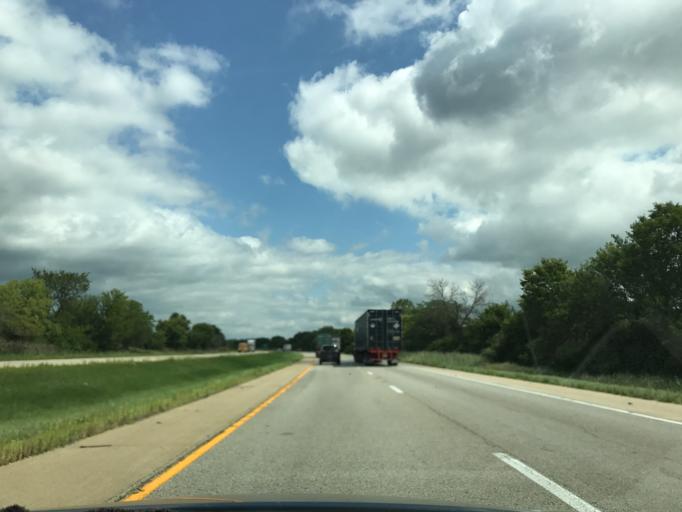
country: US
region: Illinois
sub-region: Grundy County
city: Morris
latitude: 41.3789
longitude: -88.4423
